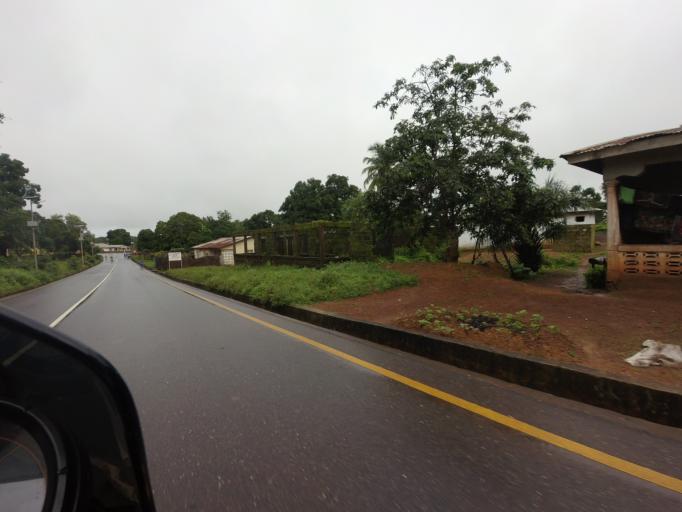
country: SL
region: Northern Province
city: Kambia
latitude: 9.1261
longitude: -12.9167
